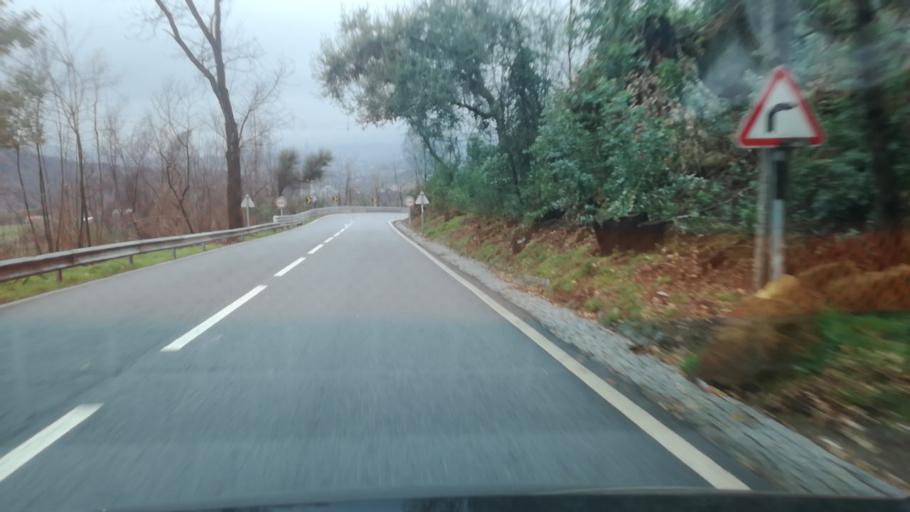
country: PT
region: Braga
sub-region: Braga
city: Braga
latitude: 41.5296
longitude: -8.3910
